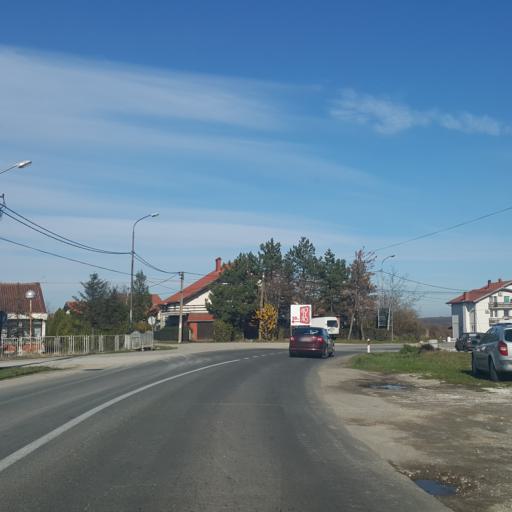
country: RS
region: Central Serbia
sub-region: Sumadijski Okrug
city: Topola
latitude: 44.2652
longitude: 20.6865
